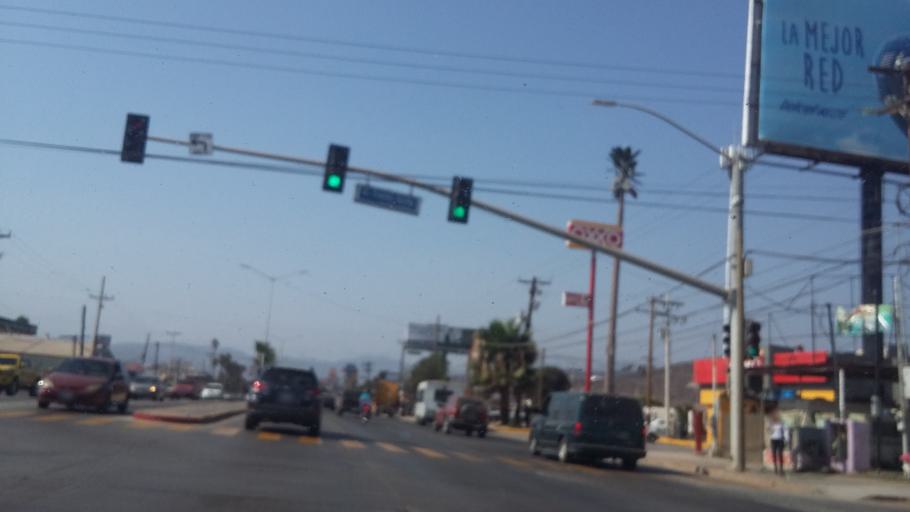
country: MX
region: Baja California
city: Ensenada
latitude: 31.8098
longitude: -116.5965
